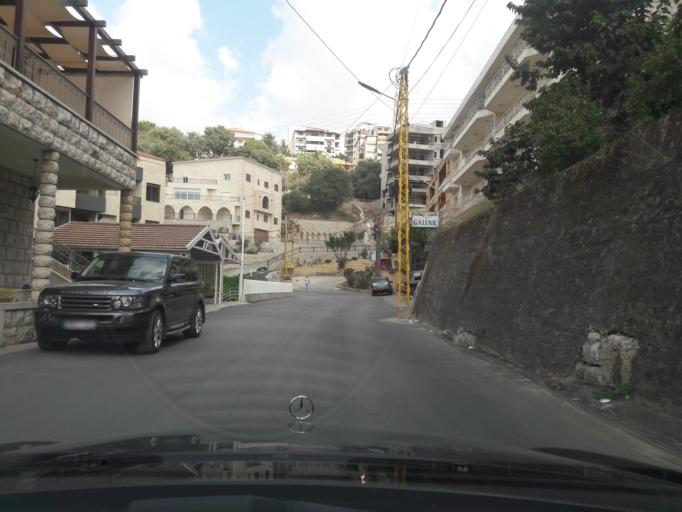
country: LB
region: Mont-Liban
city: Djounie
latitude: 33.9347
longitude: 35.6514
